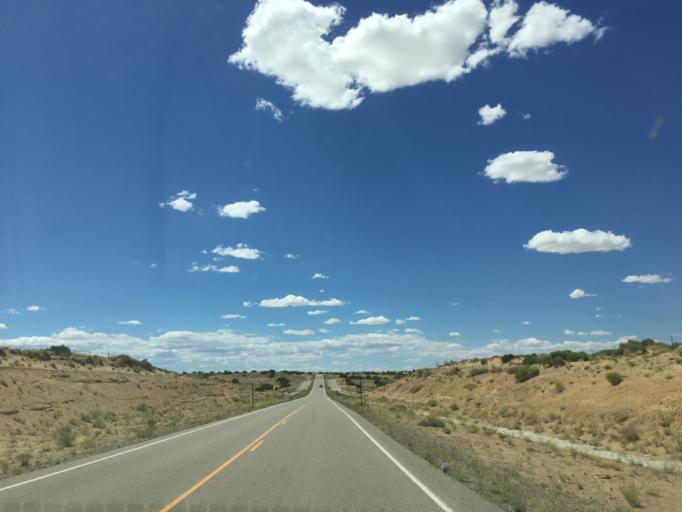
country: US
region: New Mexico
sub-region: San Juan County
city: Upper Fruitland
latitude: 36.4365
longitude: -108.2928
